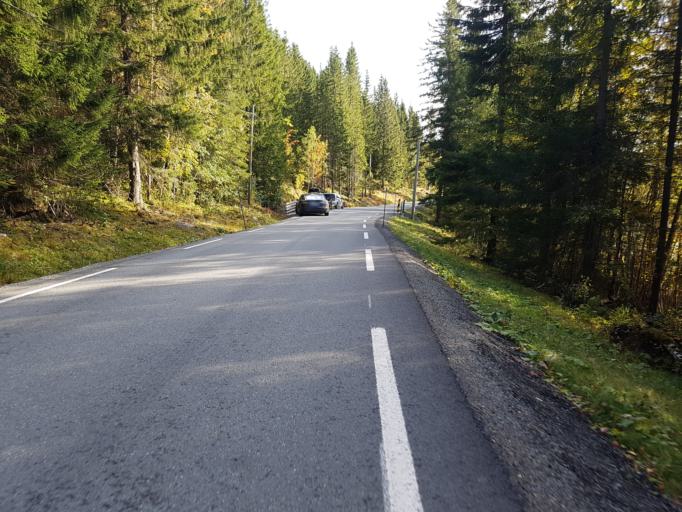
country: NO
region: Sor-Trondelag
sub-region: Malvik
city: Malvik
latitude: 63.3620
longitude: 10.6291
